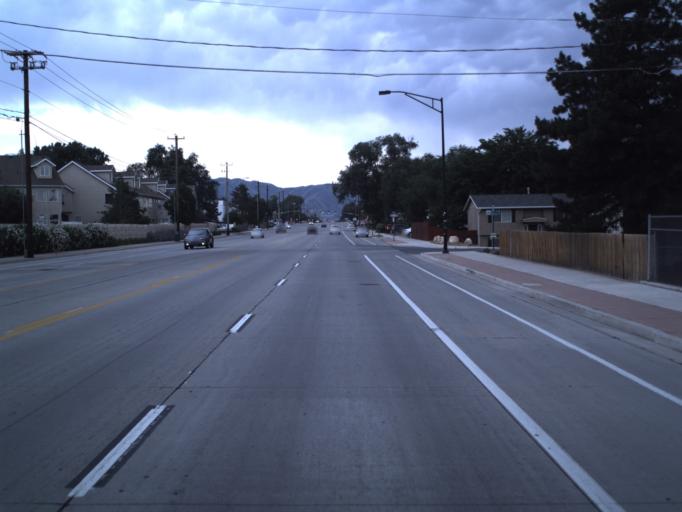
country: US
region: Utah
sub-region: Salt Lake County
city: White City
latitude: 40.5626
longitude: -111.8722
